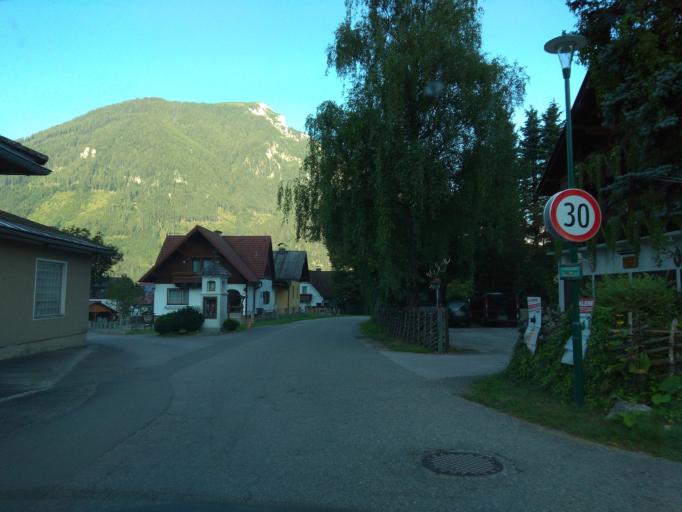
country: AT
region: Styria
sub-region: Politischer Bezirk Bruck-Muerzzuschlag
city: Sankt Ilgen
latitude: 47.5328
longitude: 15.0777
